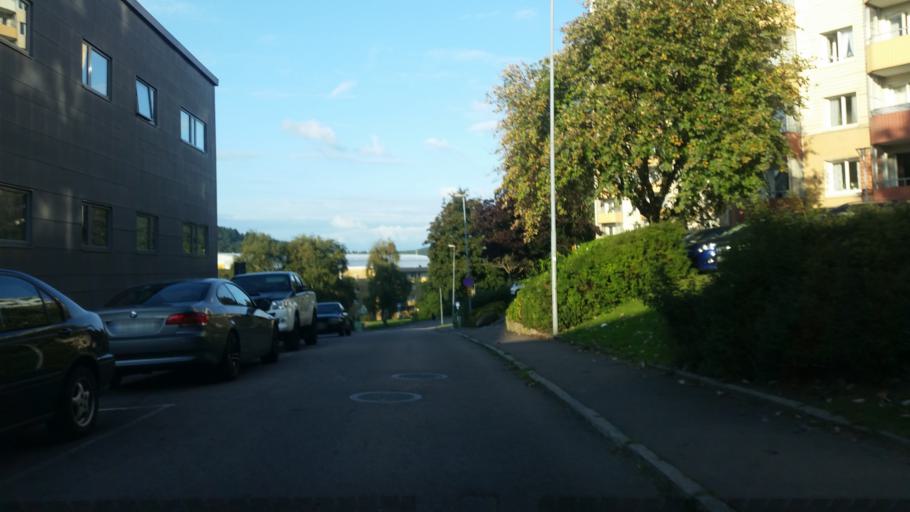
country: SE
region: Vaestra Goetaland
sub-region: Partille Kommun
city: Partille
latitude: 57.7373
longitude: 12.1128
